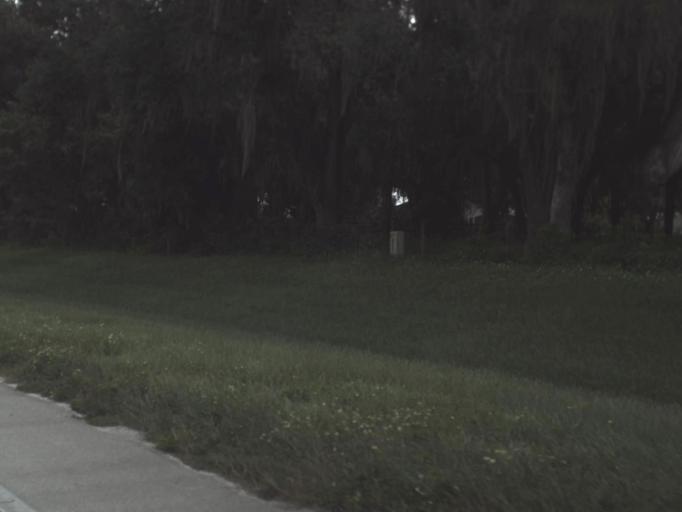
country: US
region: Florida
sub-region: DeSoto County
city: Southeast Arcadia
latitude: 27.2088
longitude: -81.8101
